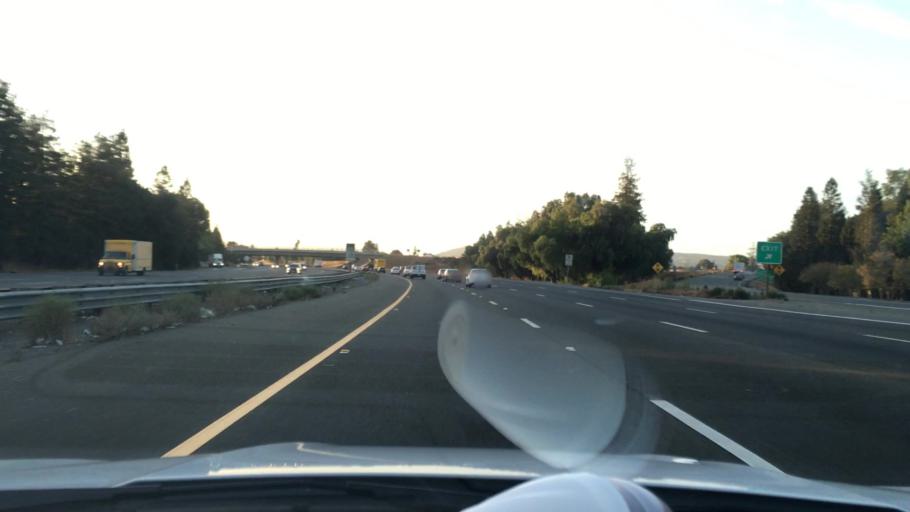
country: US
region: California
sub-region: Santa Clara County
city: Seven Trees
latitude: 37.2609
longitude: -121.7997
